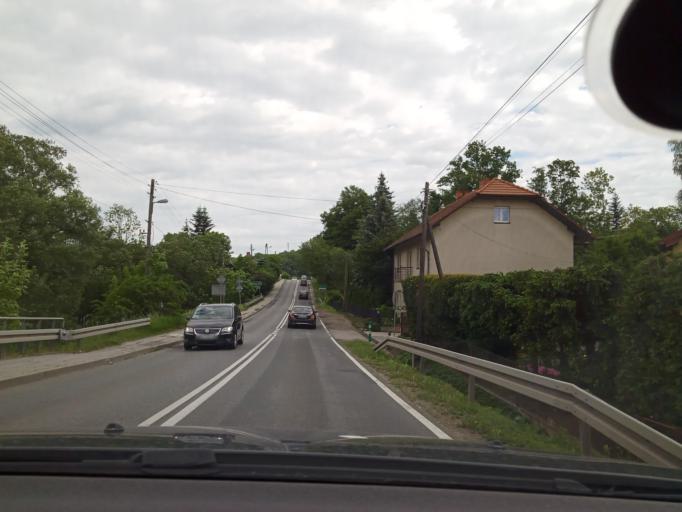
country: PL
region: Lesser Poland Voivodeship
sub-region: Powiat wielicki
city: Tomaszkowice
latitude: 49.9747
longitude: 20.1056
